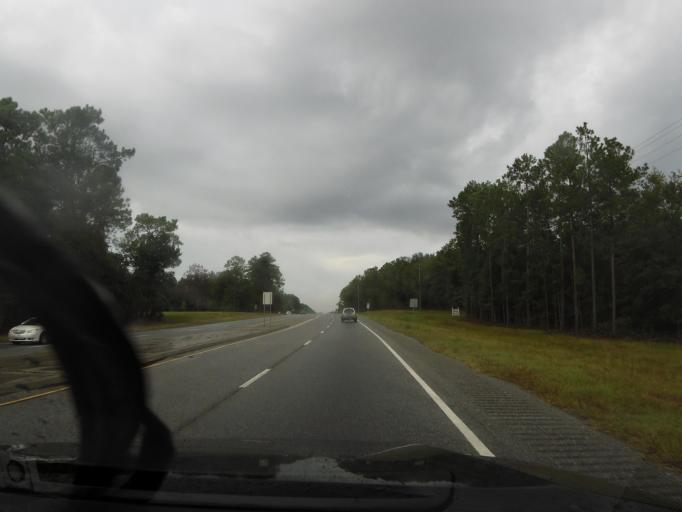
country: US
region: Georgia
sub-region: Wayne County
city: Jesup
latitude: 31.5742
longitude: -81.8455
